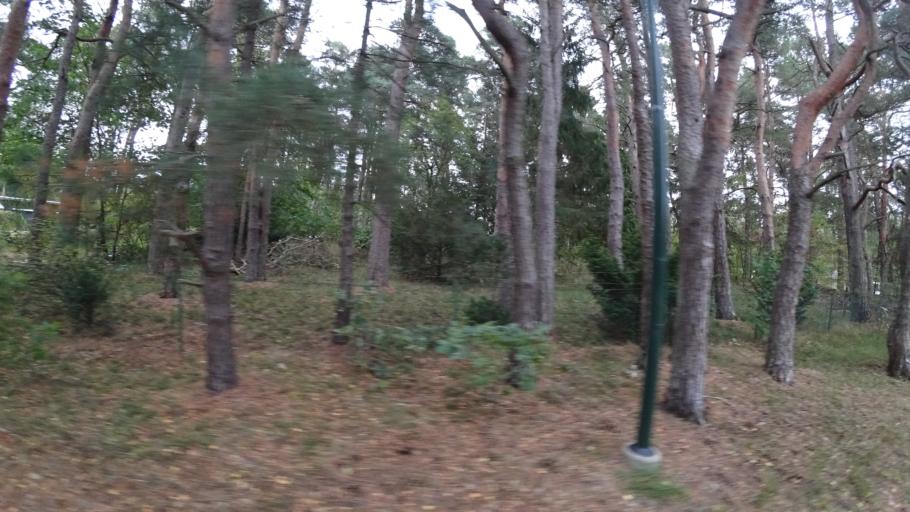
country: SE
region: Skane
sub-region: Kavlinge Kommun
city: Hofterup
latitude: 55.8162
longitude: 12.9684
